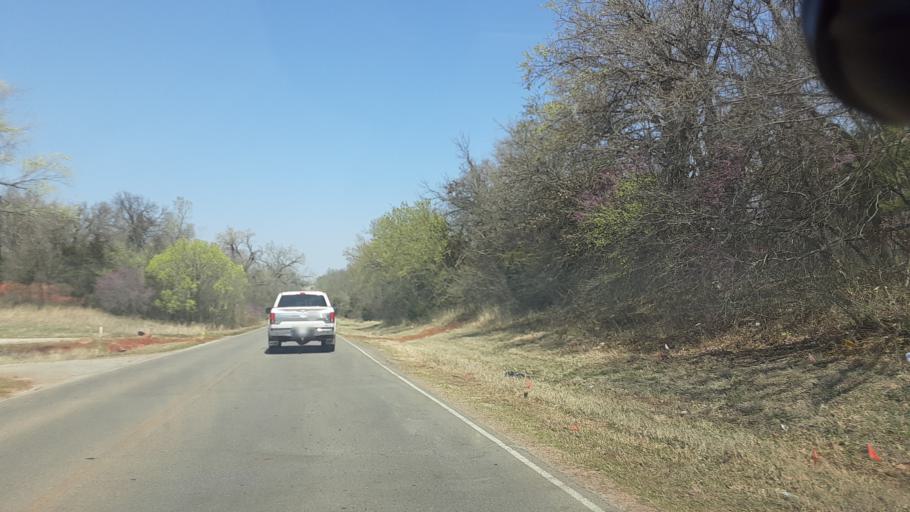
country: US
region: Oklahoma
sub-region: Oklahoma County
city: Edmond
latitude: 35.7361
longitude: -97.4784
